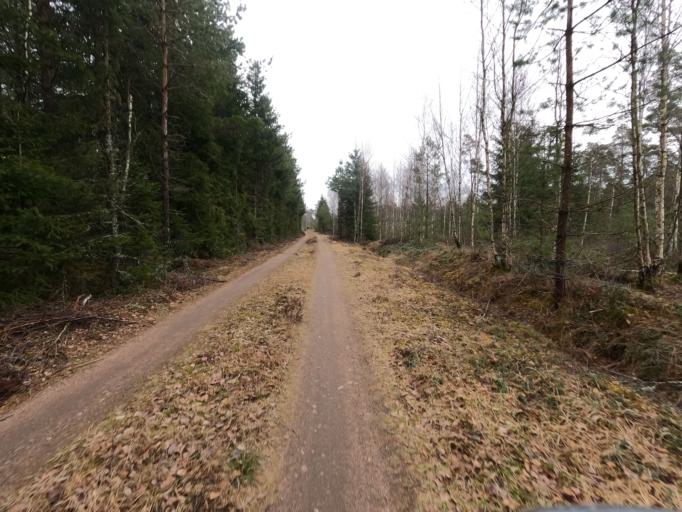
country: SE
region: Kronoberg
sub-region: Markaryds Kommun
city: Stromsnasbruk
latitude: 56.7917
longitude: 13.5987
